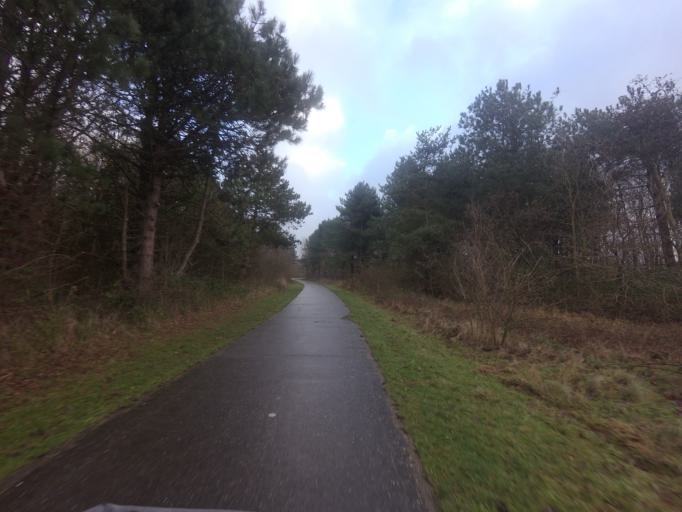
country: NL
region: North Holland
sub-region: Gemeente Texel
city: Den Burg
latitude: 53.1648
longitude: 4.8487
